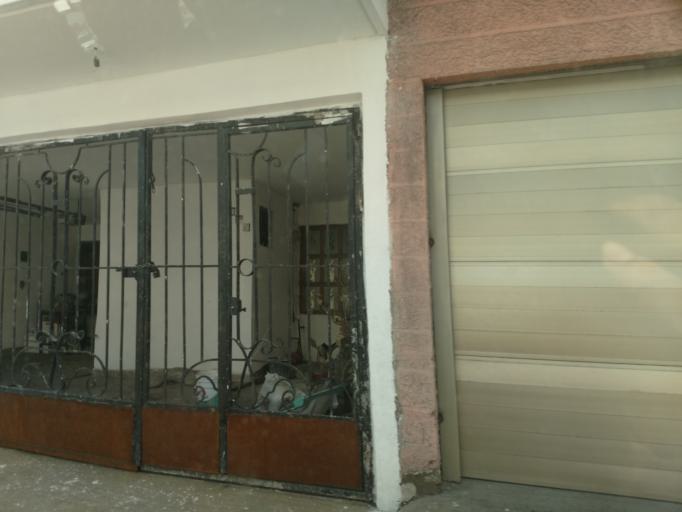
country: MX
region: Nayarit
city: Tepic
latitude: 21.4962
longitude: -104.8801
